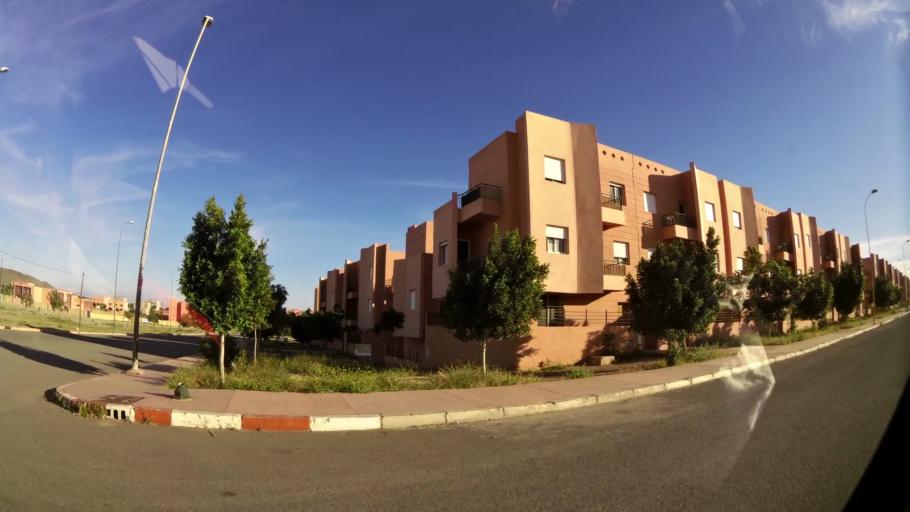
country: MA
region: Marrakech-Tensift-Al Haouz
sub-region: Marrakech
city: Marrakesh
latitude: 31.7626
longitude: -8.0999
